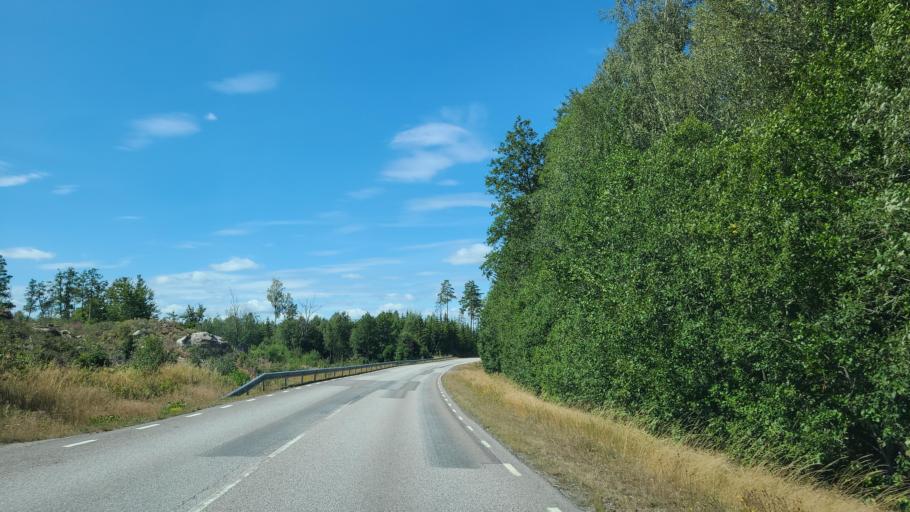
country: SE
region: Kalmar
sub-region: Emmaboda Kommun
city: Emmaboda
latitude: 56.5569
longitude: 15.7466
